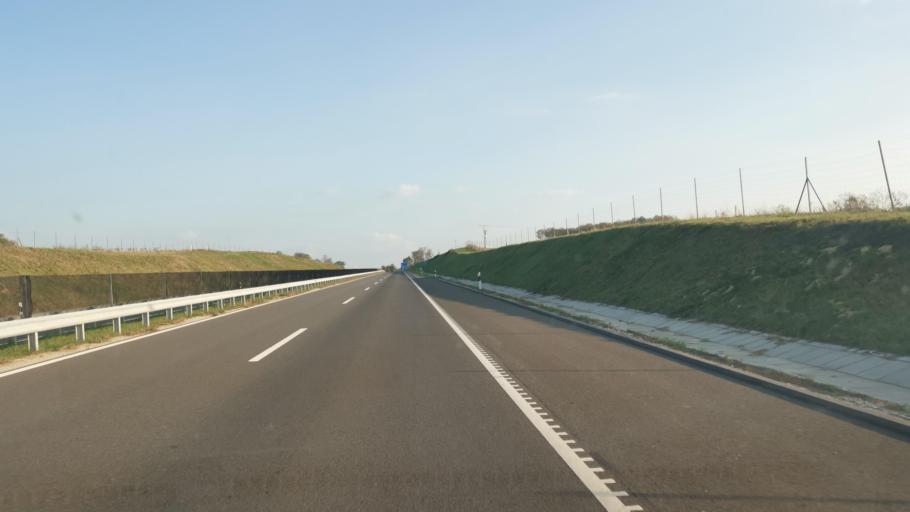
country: HU
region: Gyor-Moson-Sopron
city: Fertoszentmiklos
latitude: 47.5622
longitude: 16.8636
